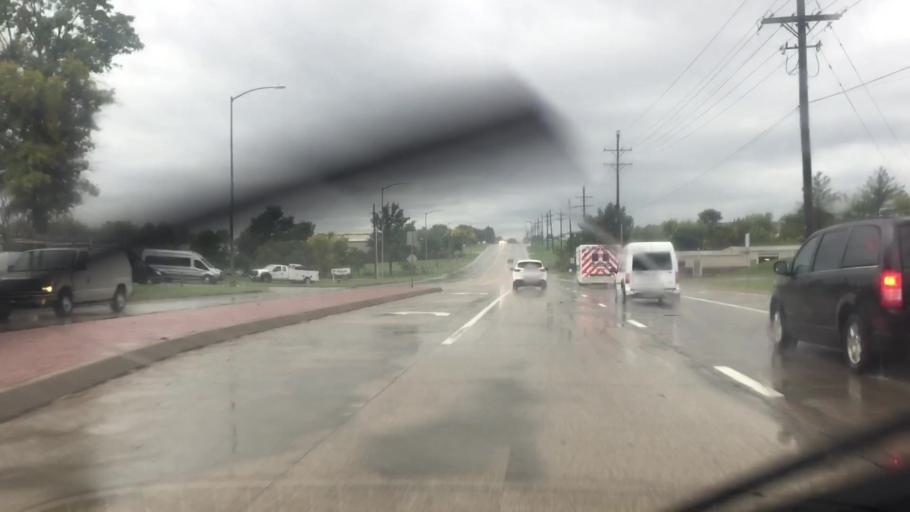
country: US
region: Kansas
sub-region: Johnson County
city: Olathe
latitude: 38.8487
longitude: -94.8159
